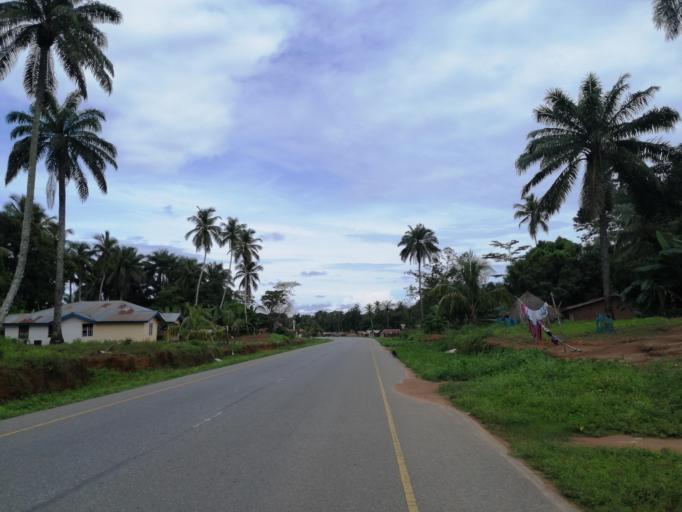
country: SL
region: Northern Province
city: Port Loko
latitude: 8.7655
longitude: -12.9047
